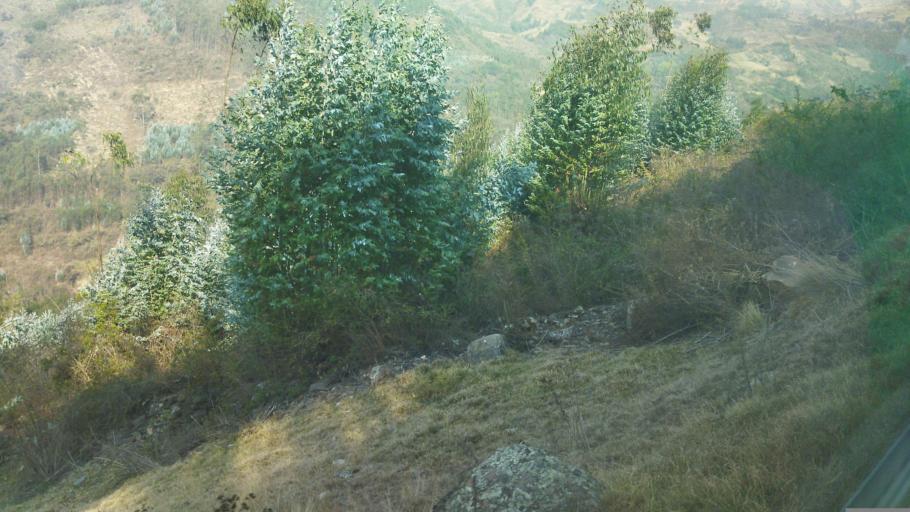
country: BO
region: La Paz
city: Quime
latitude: -16.9815
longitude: -67.1960
